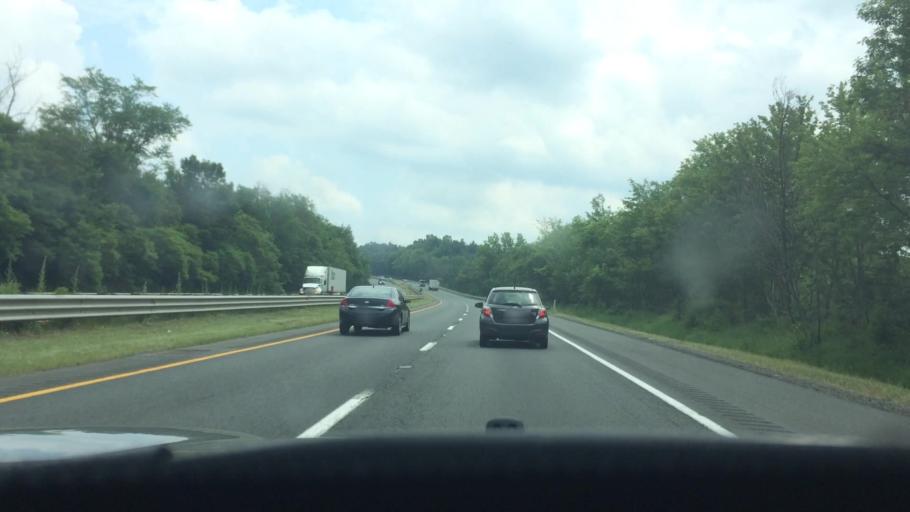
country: US
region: Massachusetts
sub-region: Worcester County
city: Fiskdale
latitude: 42.1370
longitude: -72.1300
